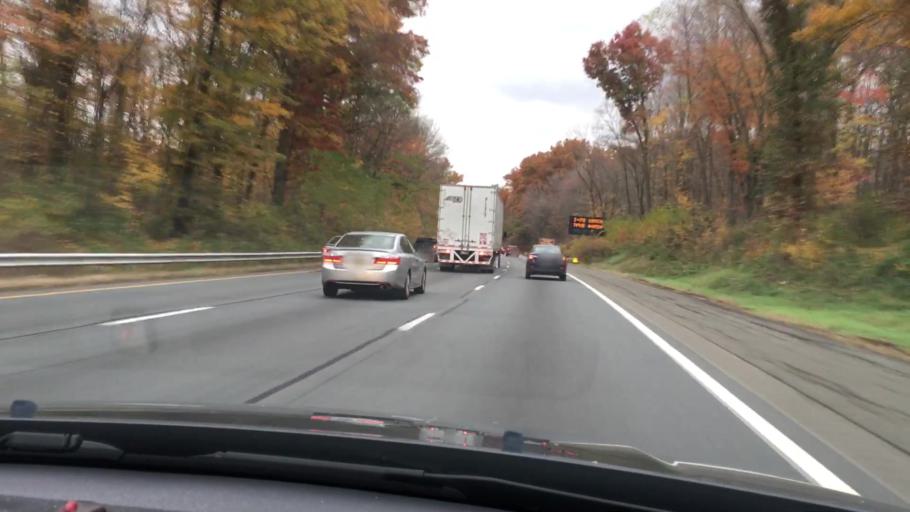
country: US
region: New Jersey
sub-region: Somerset County
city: Bernardsville
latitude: 40.7434
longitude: -74.5331
